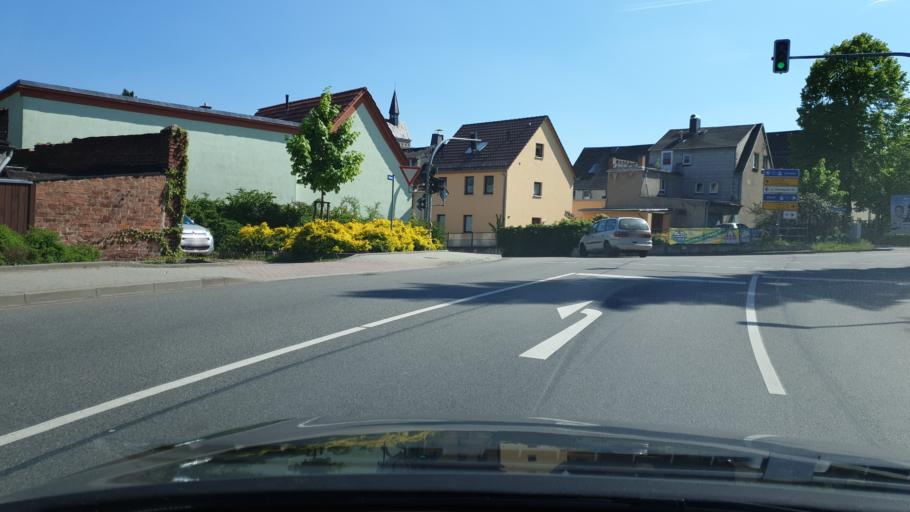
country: DE
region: Saxony
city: Mittweida
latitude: 50.9844
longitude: 12.9871
